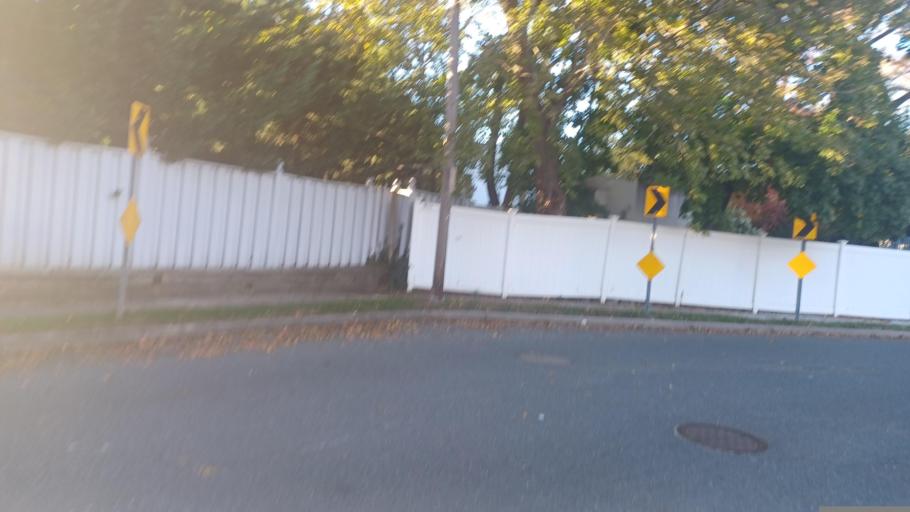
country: US
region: New York
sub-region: Nassau County
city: Oceanside
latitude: 40.6275
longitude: -73.6425
